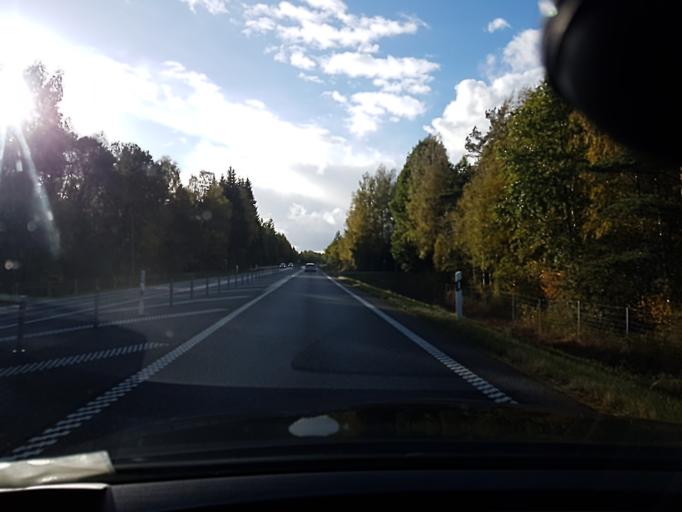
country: SE
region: Kronoberg
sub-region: Ljungby Kommun
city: Lagan
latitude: 56.8514
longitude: 14.0383
